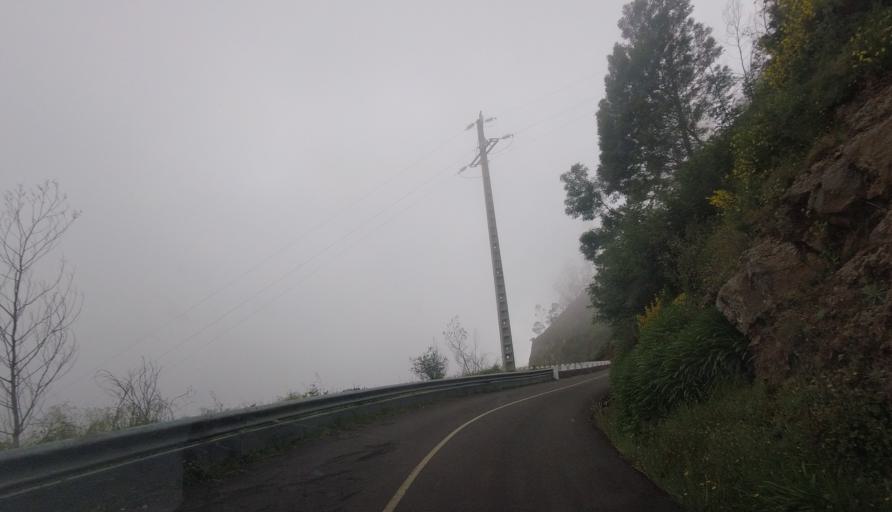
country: PT
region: Madeira
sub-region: Funchal
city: Nossa Senhora do Monte
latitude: 32.6868
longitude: -16.8978
